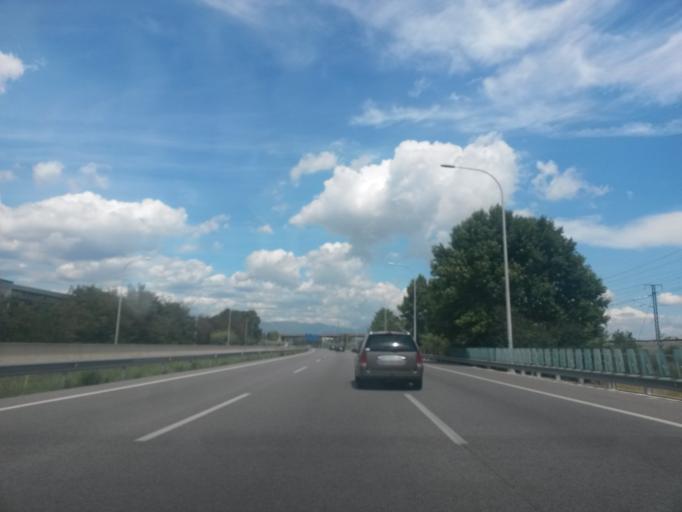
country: ES
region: Catalonia
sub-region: Provincia de Barcelona
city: Mollet del Valles
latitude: 41.5360
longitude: 2.2241
